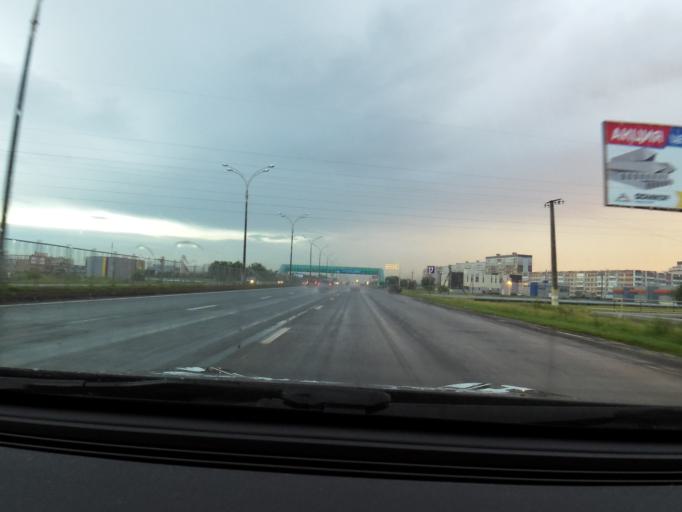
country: RU
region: Tatarstan
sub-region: Tukayevskiy Rayon
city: Naberezhnyye Chelny
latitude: 55.6870
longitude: 52.3521
